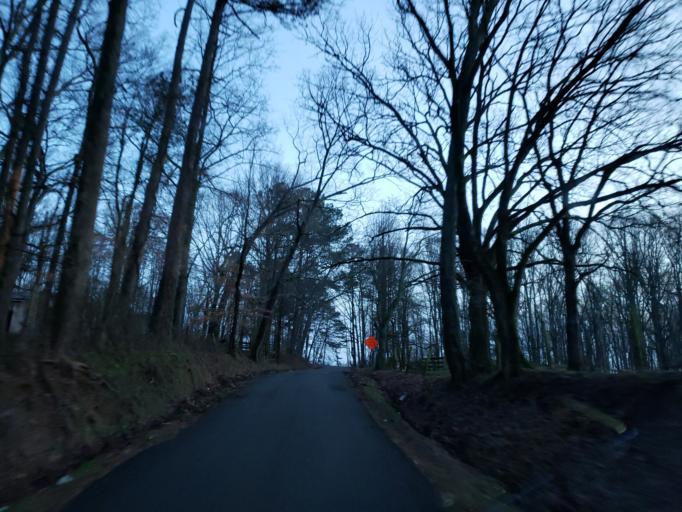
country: US
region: Georgia
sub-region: Cherokee County
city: Ball Ground
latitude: 34.2895
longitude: -84.2810
